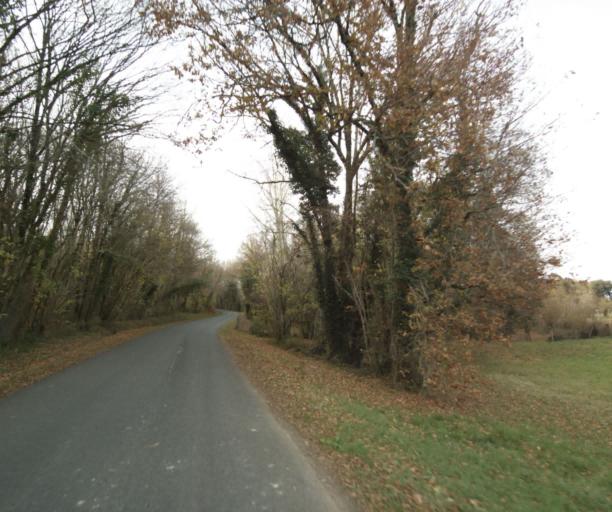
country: FR
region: Poitou-Charentes
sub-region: Departement de la Charente-Maritime
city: Saint-Hilaire-de-Villefranche
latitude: 45.8135
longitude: -0.5632
